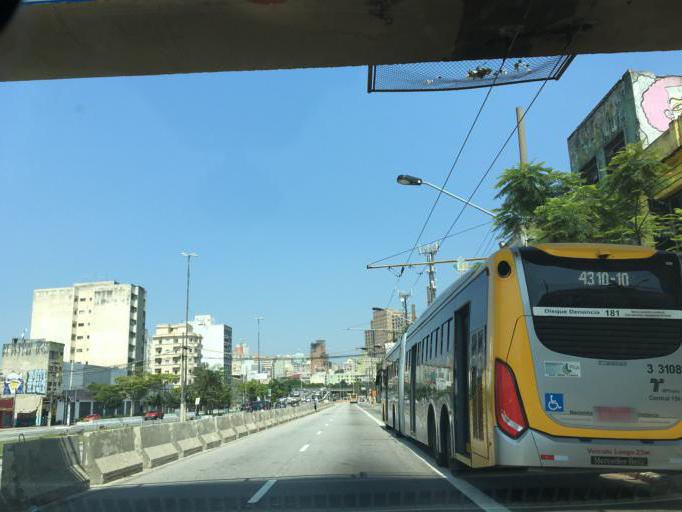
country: BR
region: Sao Paulo
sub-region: Sao Paulo
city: Sao Paulo
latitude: -23.5519
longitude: -46.6217
